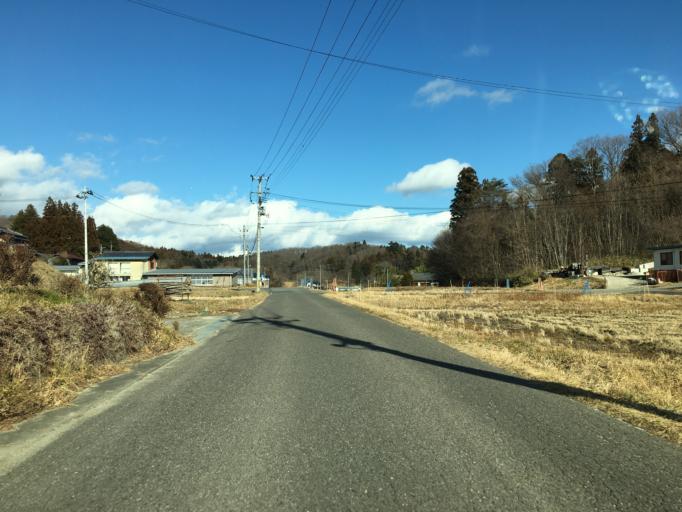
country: JP
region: Fukushima
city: Funehikimachi-funehiki
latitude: 37.4132
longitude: 140.5705
